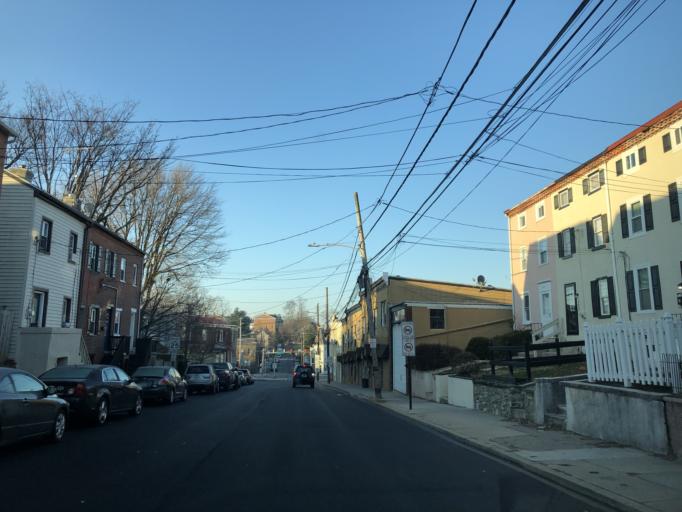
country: US
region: Pennsylvania
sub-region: Chester County
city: West Chester
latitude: 39.9596
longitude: -75.6102
